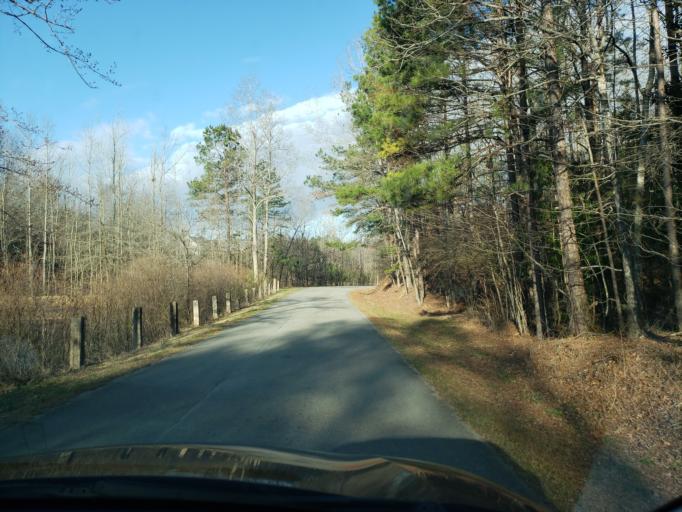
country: US
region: Alabama
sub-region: Cleburne County
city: Heflin
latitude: 33.6348
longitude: -85.5984
